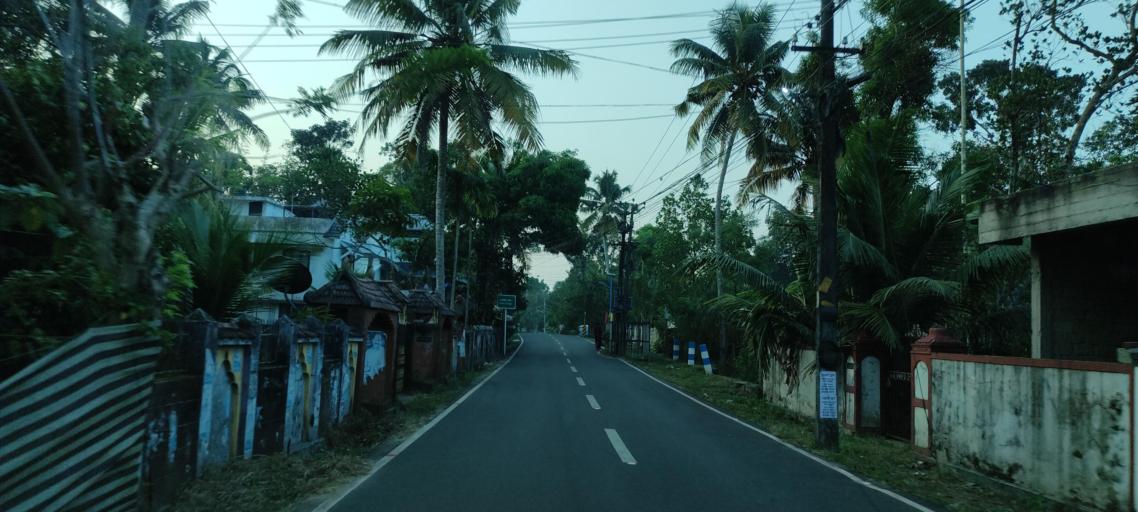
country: IN
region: Kerala
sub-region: Alappuzha
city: Alleppey
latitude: 9.4442
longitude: 76.3462
